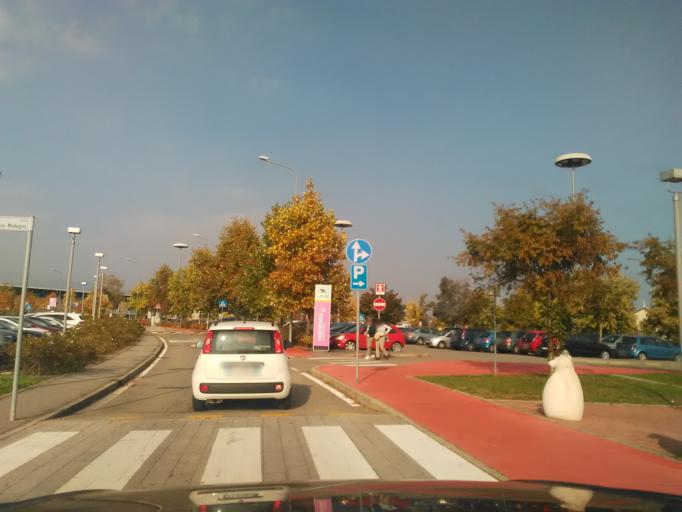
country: IT
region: Piedmont
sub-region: Provincia di Biella
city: Gaglianico
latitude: 45.5480
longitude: 8.0794
